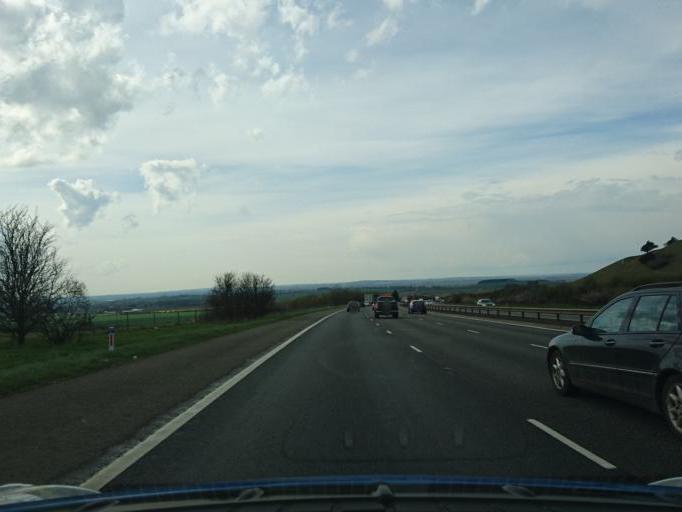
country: GB
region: England
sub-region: Buckinghamshire
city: Stokenchurch
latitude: 51.6636
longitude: -0.9486
